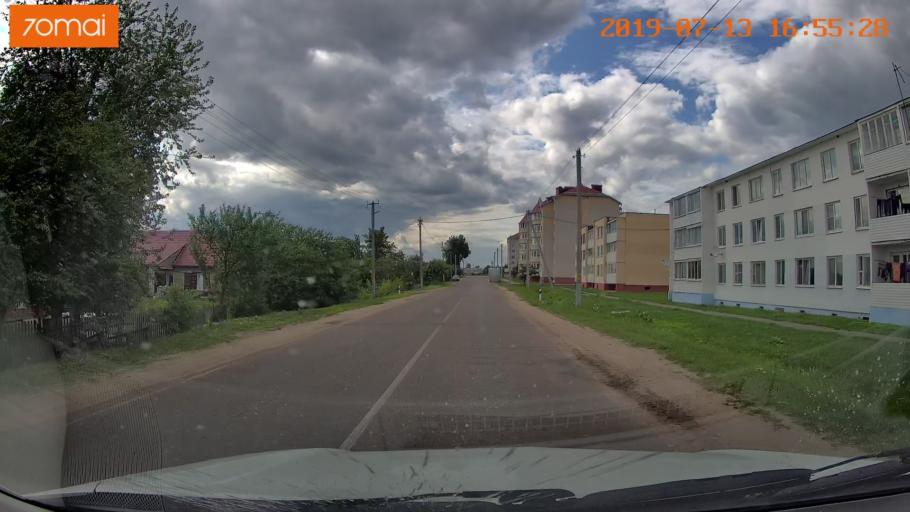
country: BY
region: Mogilev
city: Kirawsk
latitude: 53.2679
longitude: 29.4669
